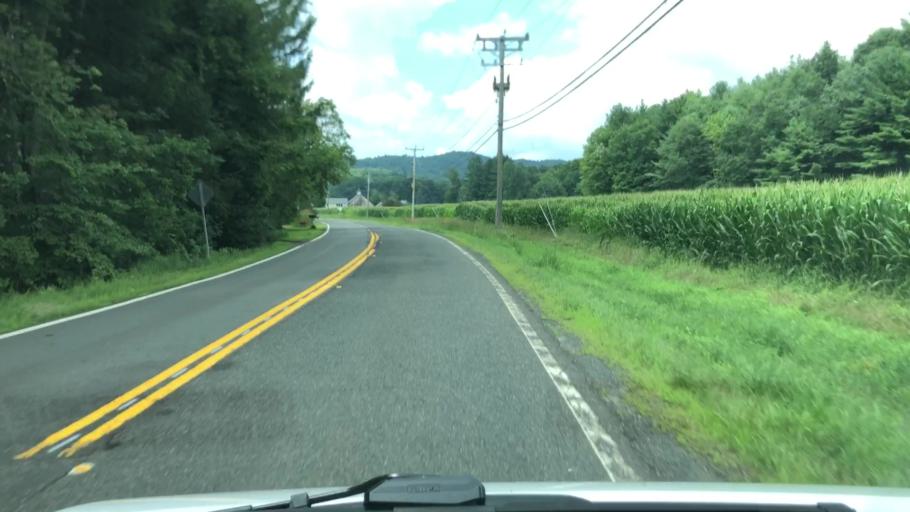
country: US
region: Massachusetts
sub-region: Franklin County
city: Conway
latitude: 42.5106
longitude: -72.7124
